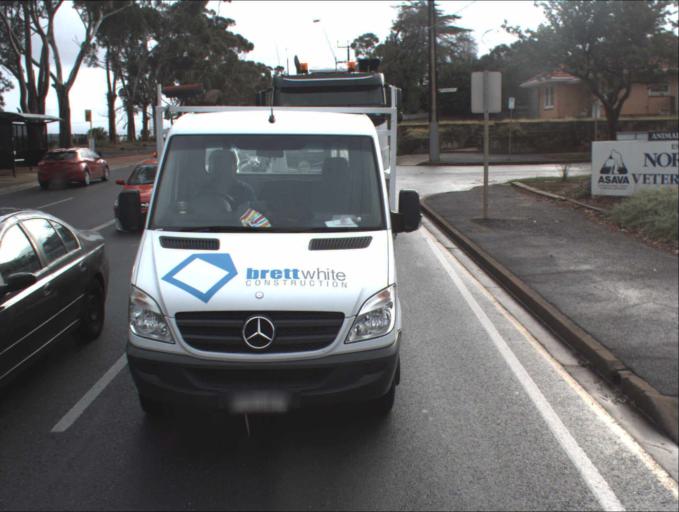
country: AU
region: South Australia
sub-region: Salisbury
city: Ingle Farm
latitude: -34.8425
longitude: 138.6209
